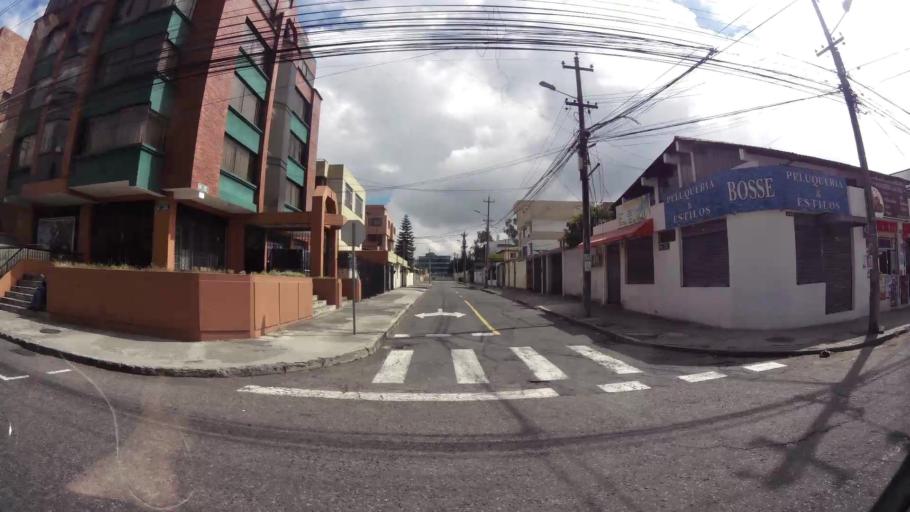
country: EC
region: Pichincha
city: Quito
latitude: -0.1532
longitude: -78.4829
